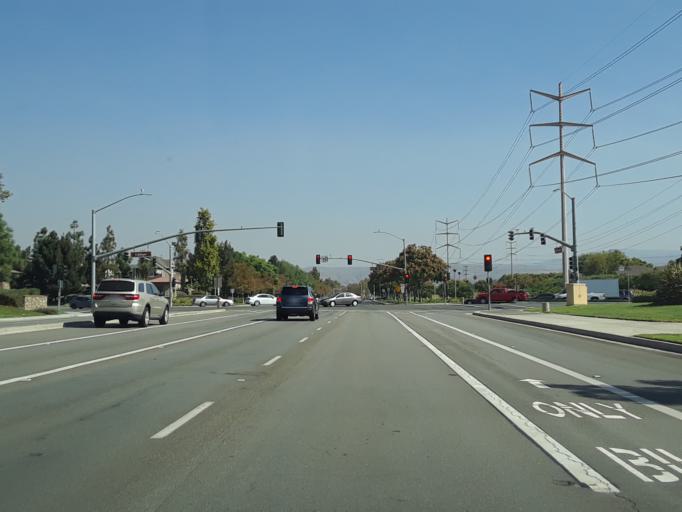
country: US
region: California
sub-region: Orange County
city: Irvine
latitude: 33.7003
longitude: -117.8031
